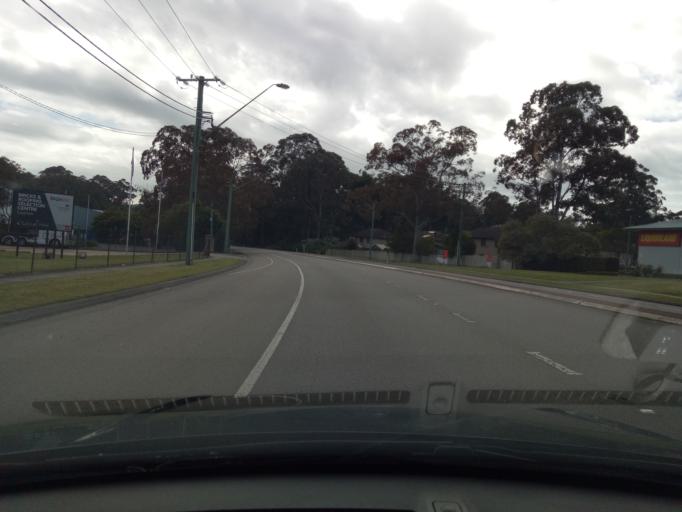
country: AU
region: New South Wales
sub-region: Gosford Shire
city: Lisarow
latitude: -33.3846
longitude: 151.3669
